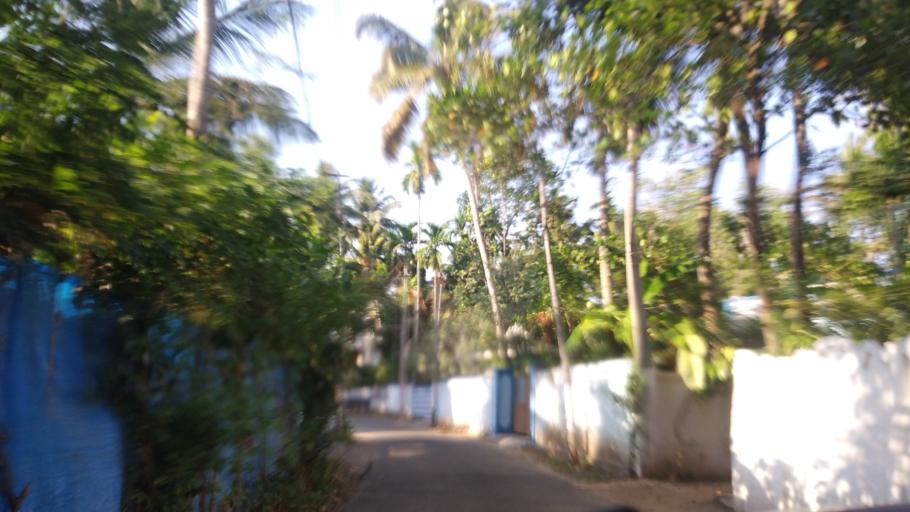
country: IN
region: Kerala
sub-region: Thrissur District
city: Kodungallur
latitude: 10.1324
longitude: 76.2018
